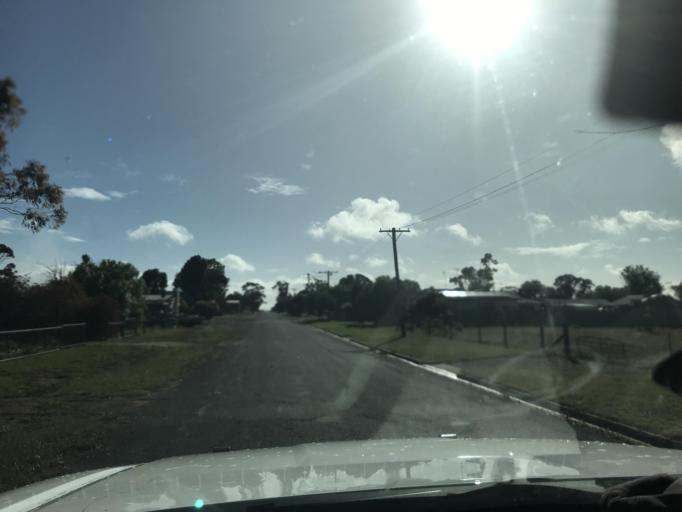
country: AU
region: Victoria
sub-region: Horsham
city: Horsham
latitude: -36.7201
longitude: 141.4716
